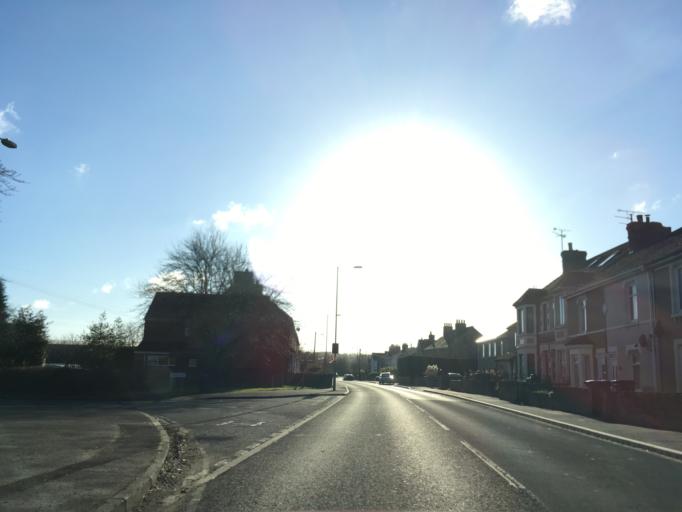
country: GB
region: England
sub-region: Borough of Swindon
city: Wroughton
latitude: 51.5340
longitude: -1.7850
